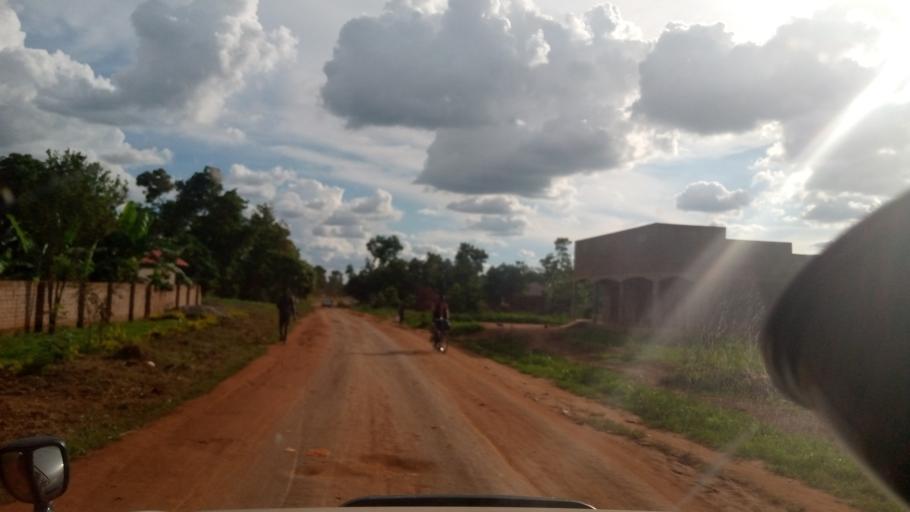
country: UG
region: Northern Region
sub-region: Lira District
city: Lira
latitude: 2.2286
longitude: 32.8996
